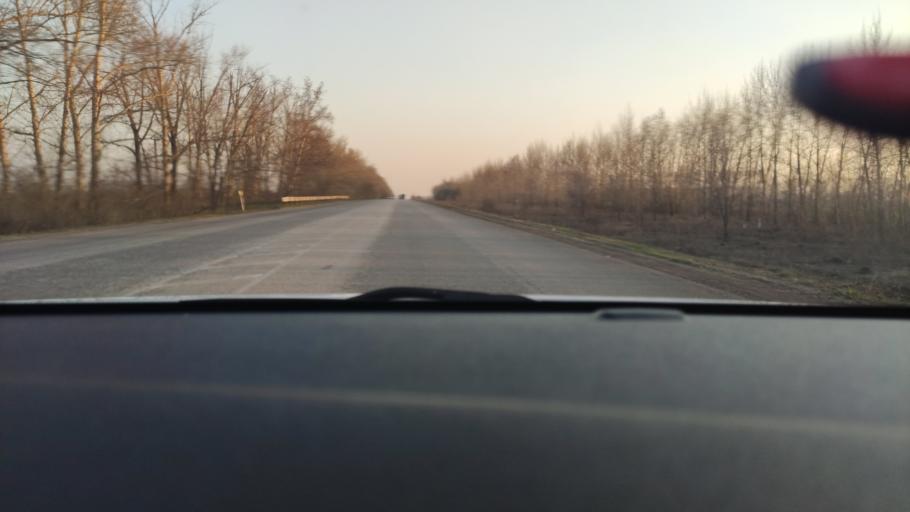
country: RU
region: Voronezj
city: Maslovka
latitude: 51.4557
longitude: 39.3041
